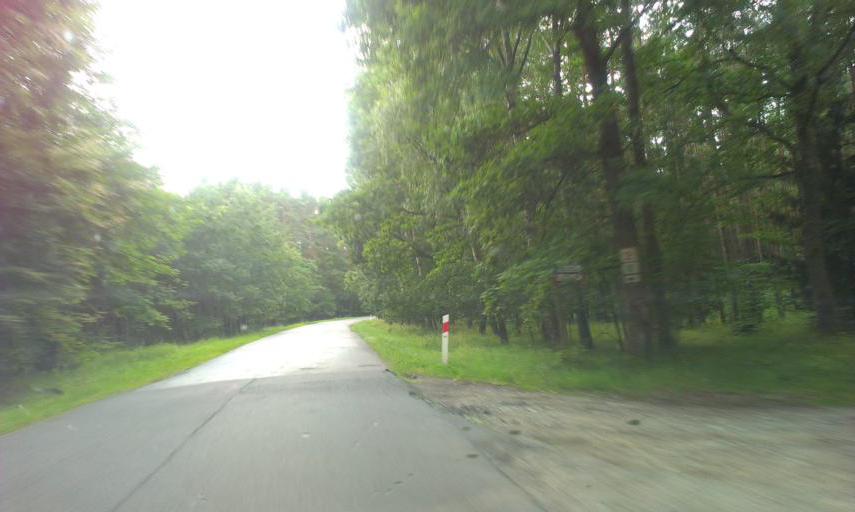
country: PL
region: West Pomeranian Voivodeship
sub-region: Powiat swidwinski
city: Polczyn-Zdroj
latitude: 53.8418
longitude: 16.1562
